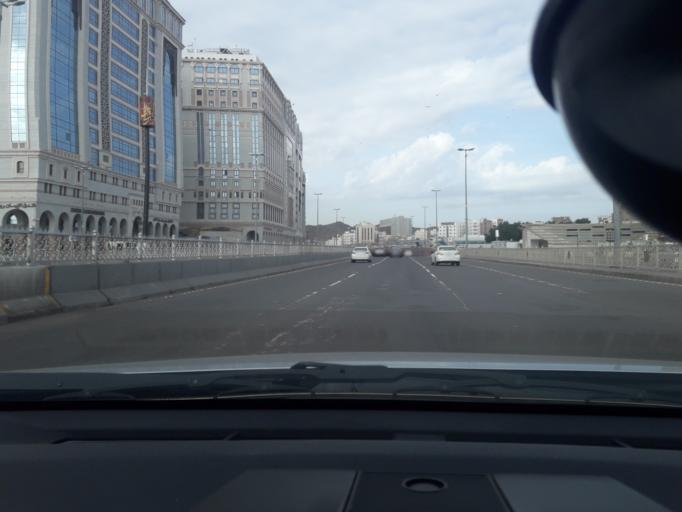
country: SA
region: Al Madinah al Munawwarah
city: Medina
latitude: 24.4736
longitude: 39.6146
